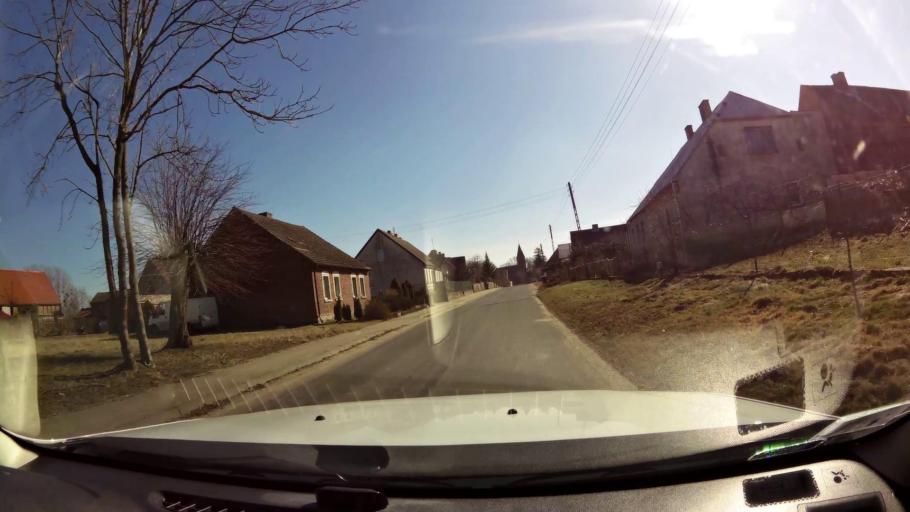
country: PL
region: West Pomeranian Voivodeship
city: Trzcinsko Zdroj
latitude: 52.9875
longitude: 14.6042
